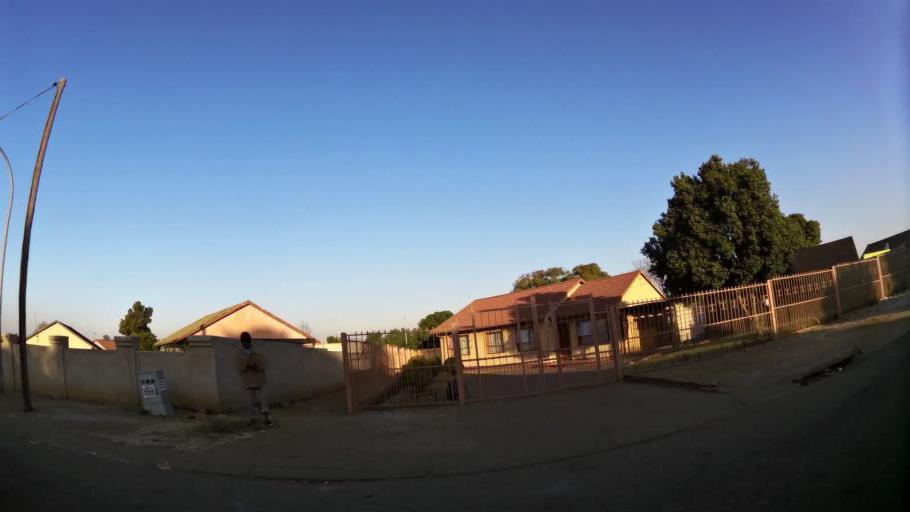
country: ZA
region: North-West
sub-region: Bojanala Platinum District Municipality
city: Rustenburg
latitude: -25.6374
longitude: 27.2062
